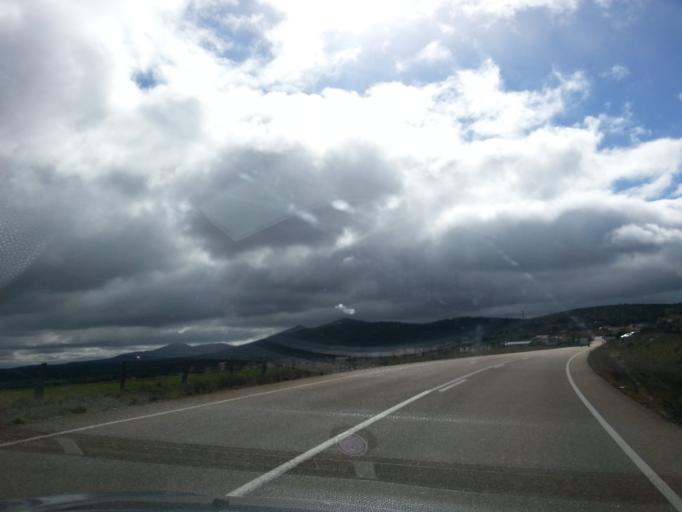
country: ES
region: Castille and Leon
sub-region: Provincia de Salamanca
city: Tamames
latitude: 40.6656
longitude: -6.1152
